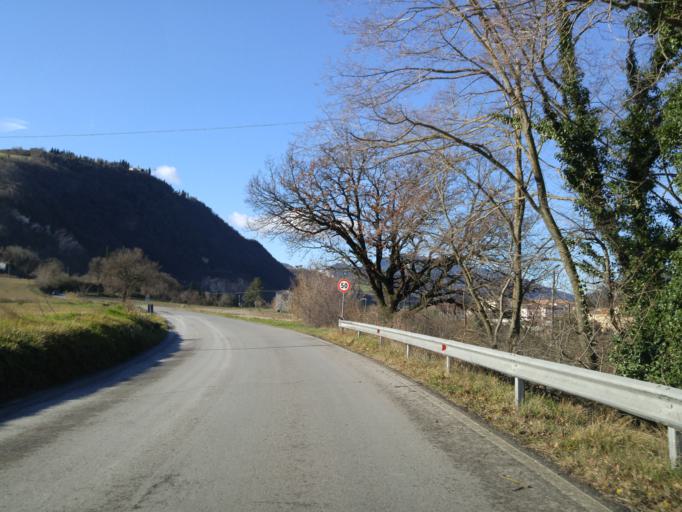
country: IT
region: The Marches
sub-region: Provincia di Pesaro e Urbino
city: Fossombrone
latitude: 43.6878
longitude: 12.8190
